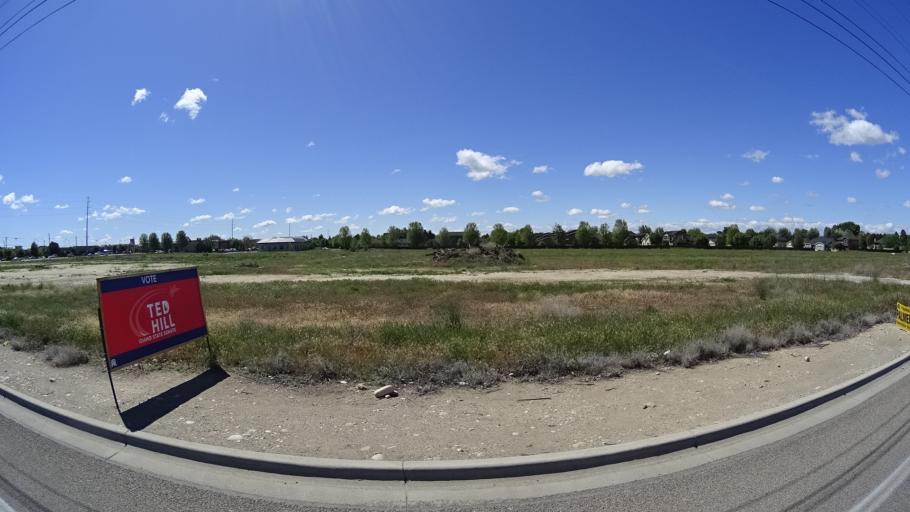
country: US
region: Idaho
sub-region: Ada County
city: Meridian
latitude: 43.6338
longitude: -116.3567
